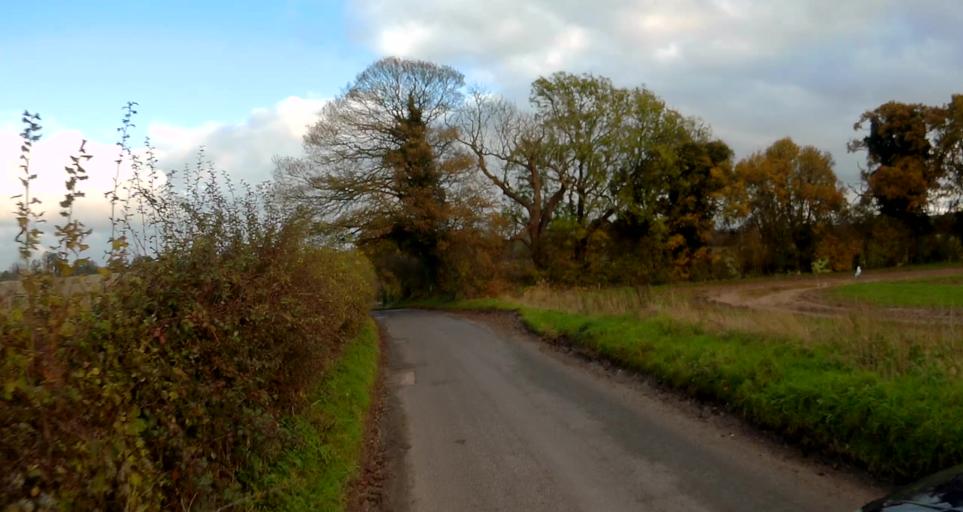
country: GB
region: England
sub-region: Hampshire
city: Long Sutton
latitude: 51.2244
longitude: -0.9819
